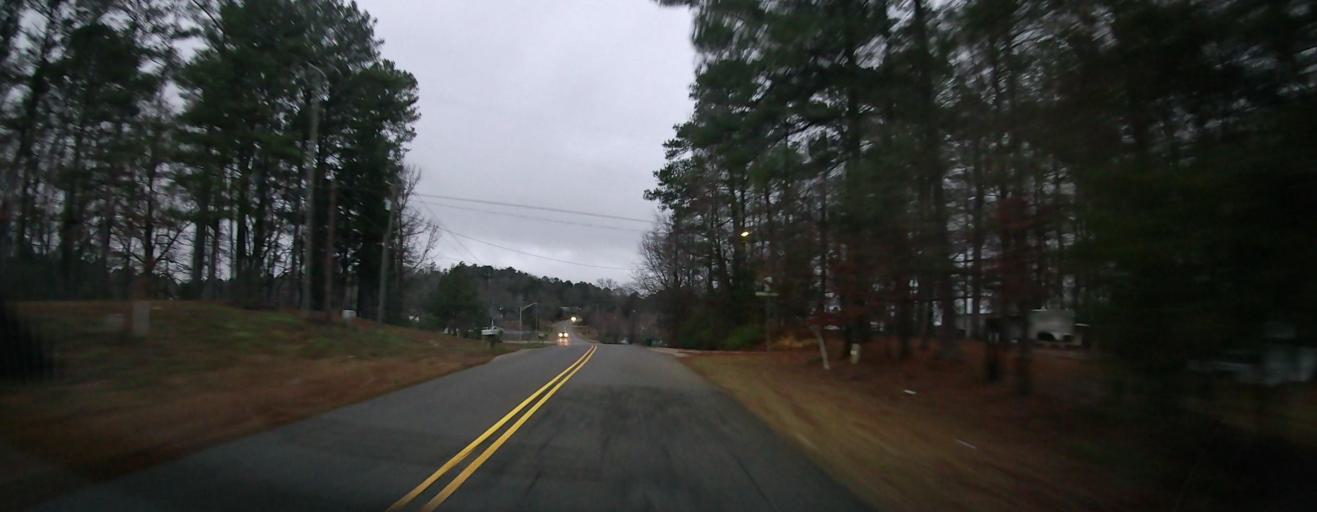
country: US
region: Alabama
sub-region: Tuscaloosa County
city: Vance
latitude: 33.1601
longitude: -87.2299
